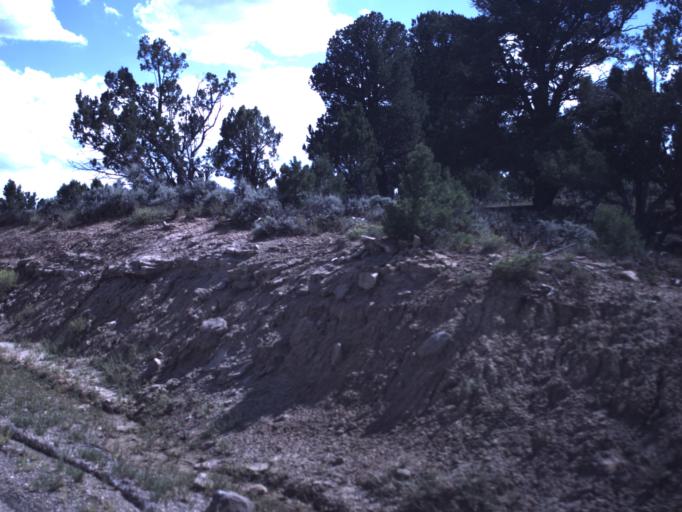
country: US
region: Utah
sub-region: Duchesne County
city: Duchesne
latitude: 40.3109
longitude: -110.6987
